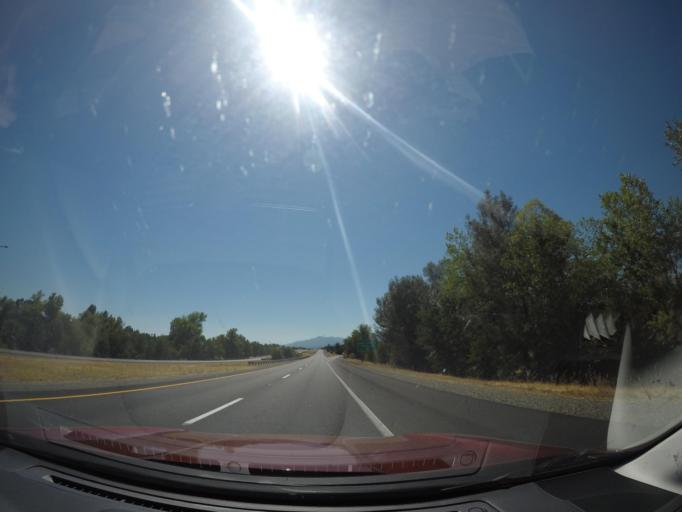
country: US
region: California
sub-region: Shasta County
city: Redding
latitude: 40.6158
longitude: -122.3449
